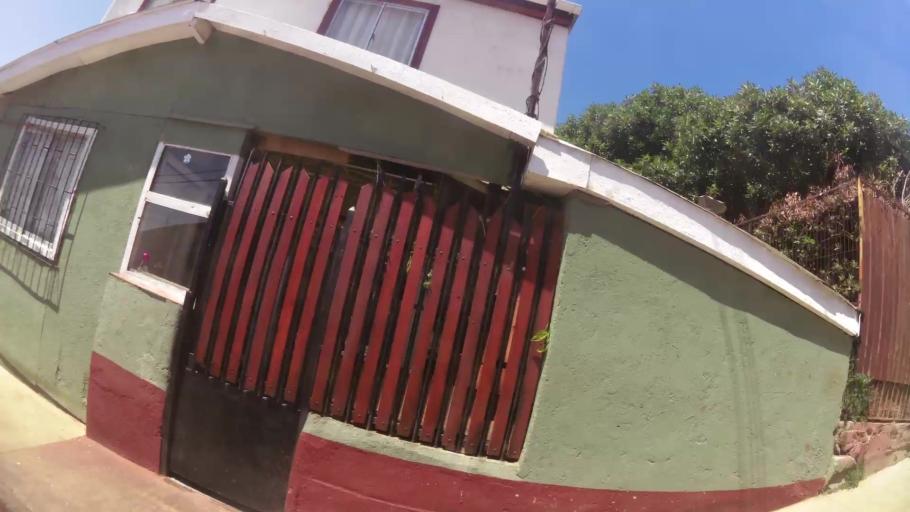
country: CL
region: Valparaiso
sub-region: Provincia de Valparaiso
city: Valparaiso
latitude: -33.0410
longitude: -71.6433
